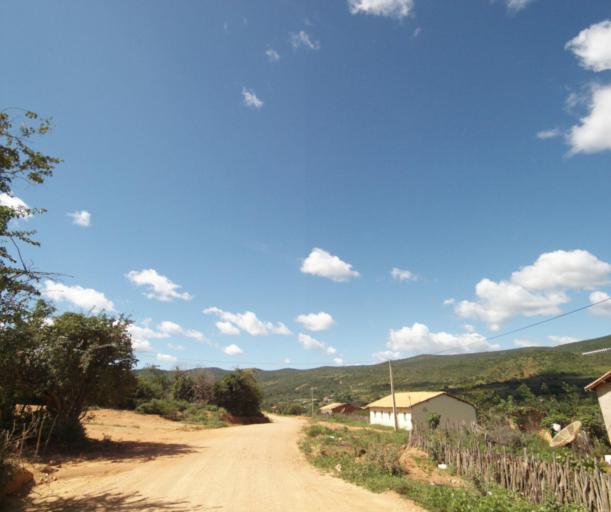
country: BR
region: Bahia
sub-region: Pocoes
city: Pocoes
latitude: -14.2580
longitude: -40.7014
